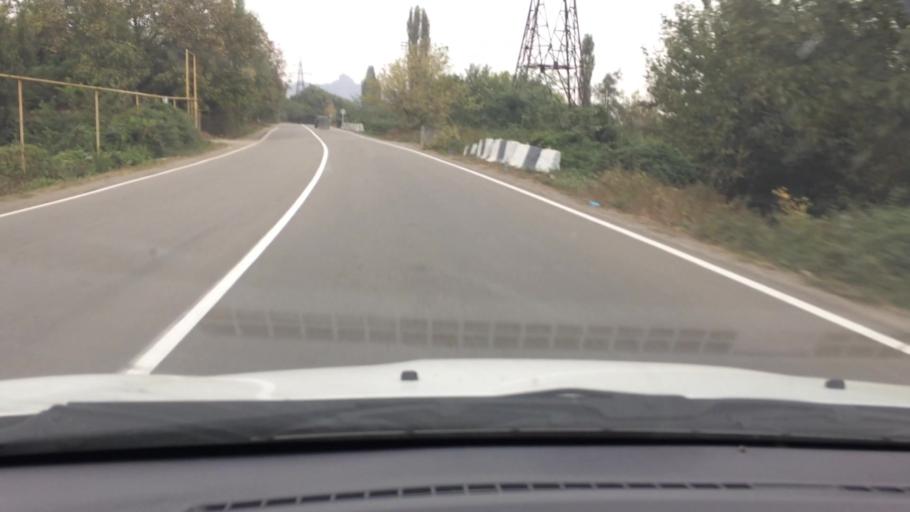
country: GE
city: Naghvarevi
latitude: 41.3236
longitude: 44.7995
